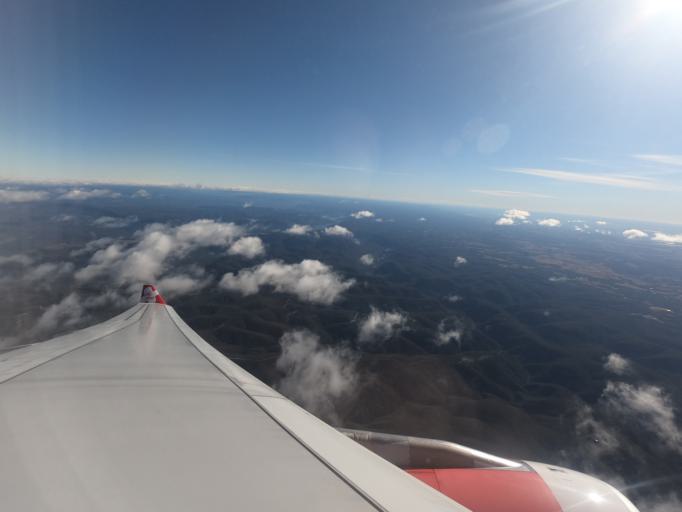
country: AU
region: New South Wales
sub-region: Wollondilly
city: Buxton
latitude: -34.2704
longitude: 150.4406
